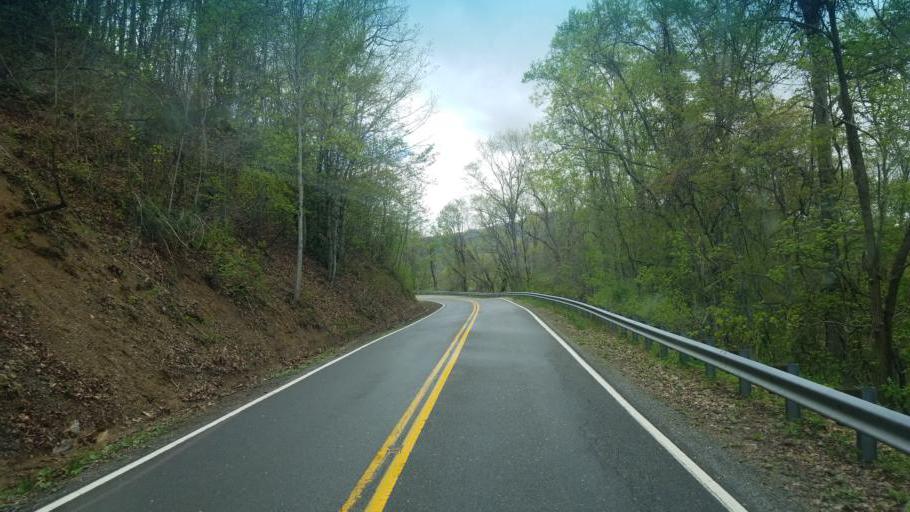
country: US
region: Virginia
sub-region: Tazewell County
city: Tazewell
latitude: 37.0057
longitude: -81.5178
